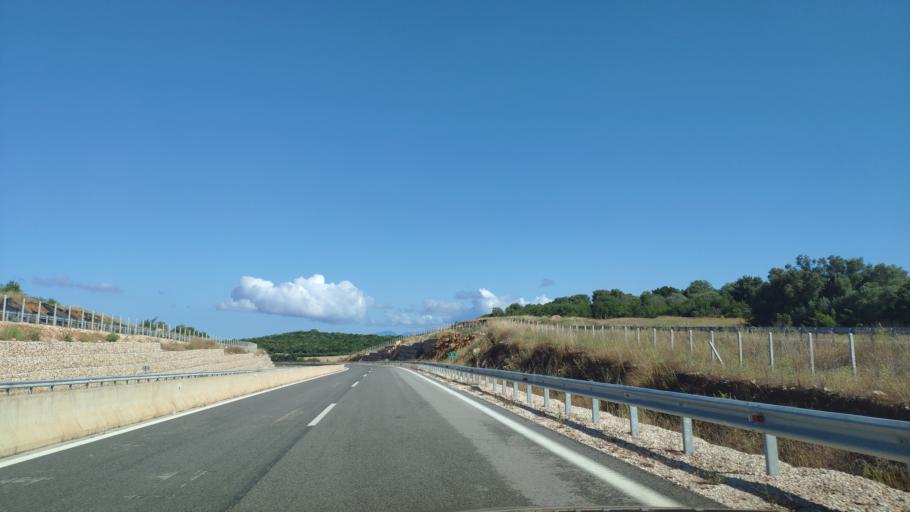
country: GR
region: West Greece
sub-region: Nomos Aitolias kai Akarnanias
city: Vonitsa
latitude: 38.9084
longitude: 20.8485
